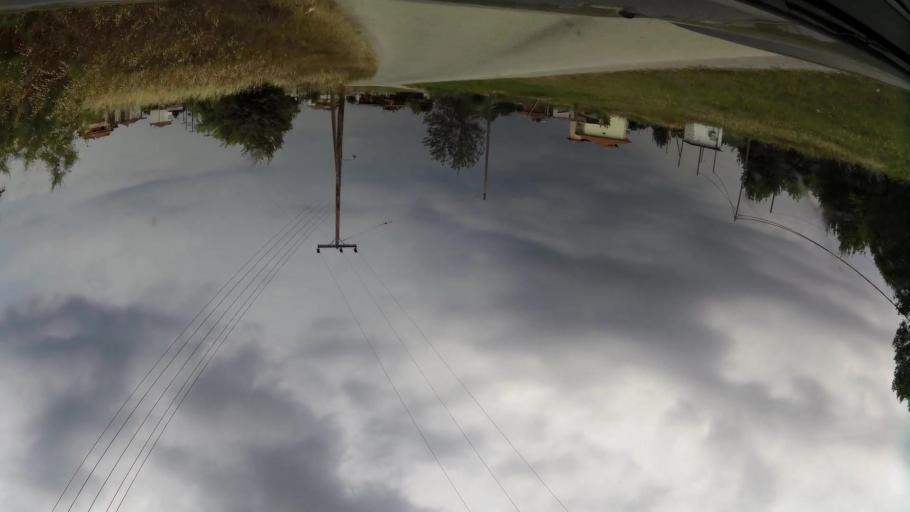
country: GR
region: Central Macedonia
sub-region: Nomos Pierias
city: Paralia
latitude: 40.2757
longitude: 22.5894
